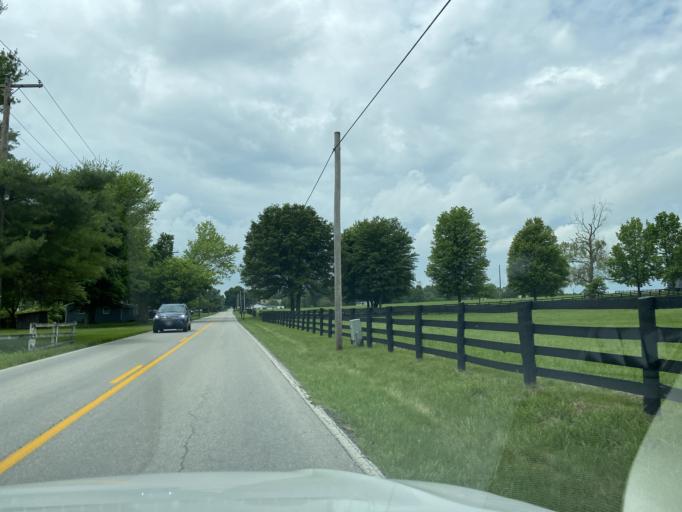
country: US
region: Kentucky
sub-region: Scott County
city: Georgetown
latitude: 38.2212
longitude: -84.4626
